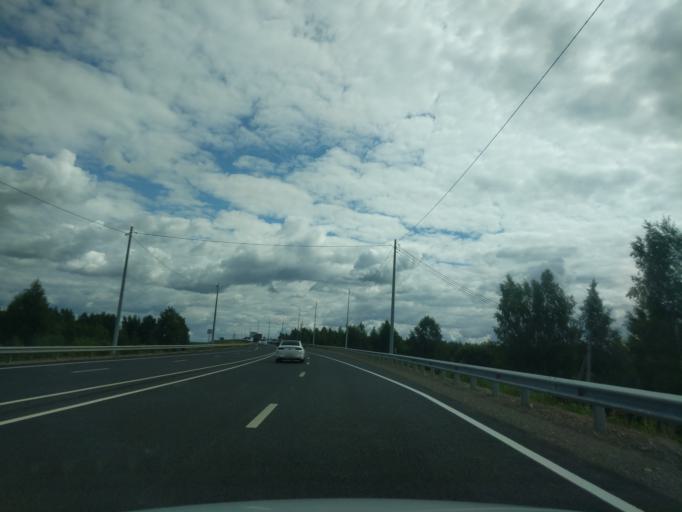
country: RU
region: Kostroma
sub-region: Kostromskoy Rayon
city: Kostroma
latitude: 57.7311
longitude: 40.8712
